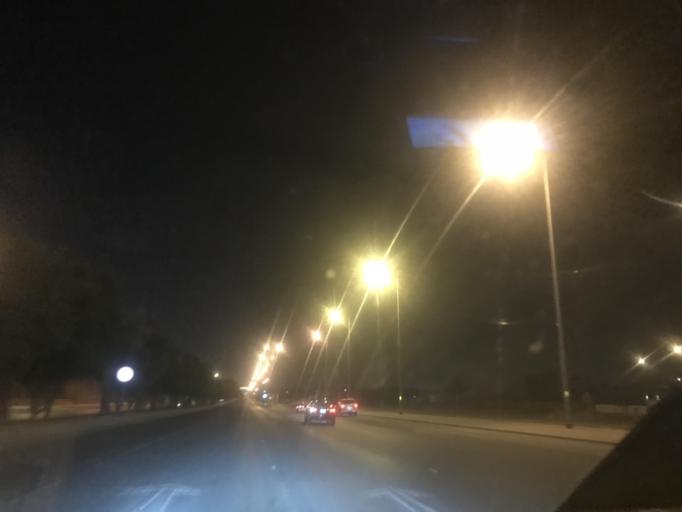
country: SA
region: Ar Riyad
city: Riyadh
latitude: 24.7946
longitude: 46.5865
